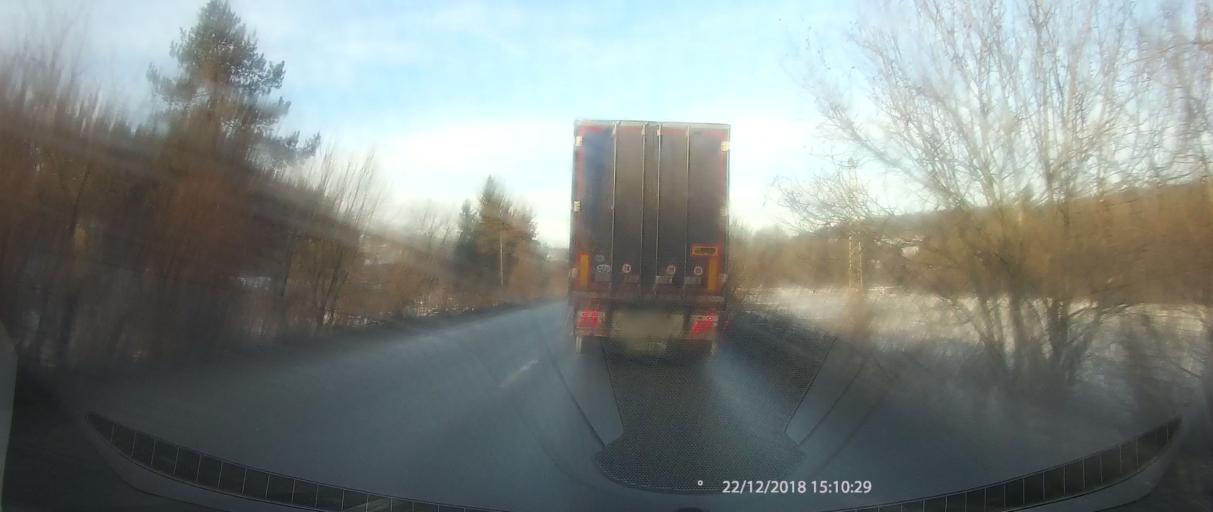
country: BG
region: Ruse
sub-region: Obshtina Borovo
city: Borovo
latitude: 43.5164
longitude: 25.7965
